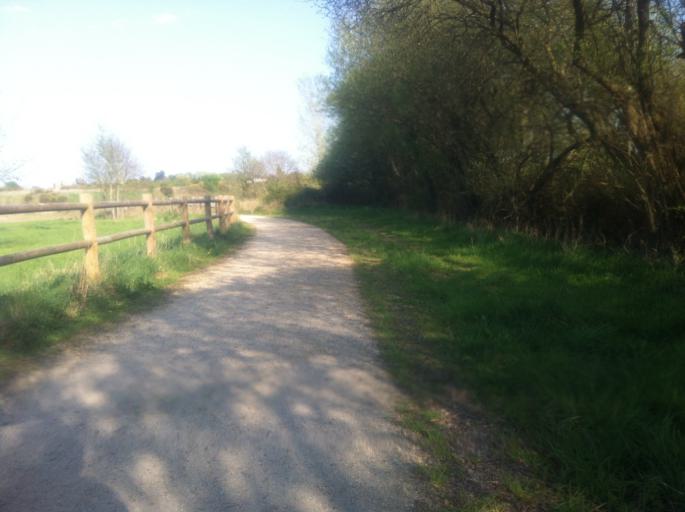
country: FR
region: Brittany
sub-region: Departement d'Ille-et-Vilaine
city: Bruz
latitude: 48.0119
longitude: -1.7197
